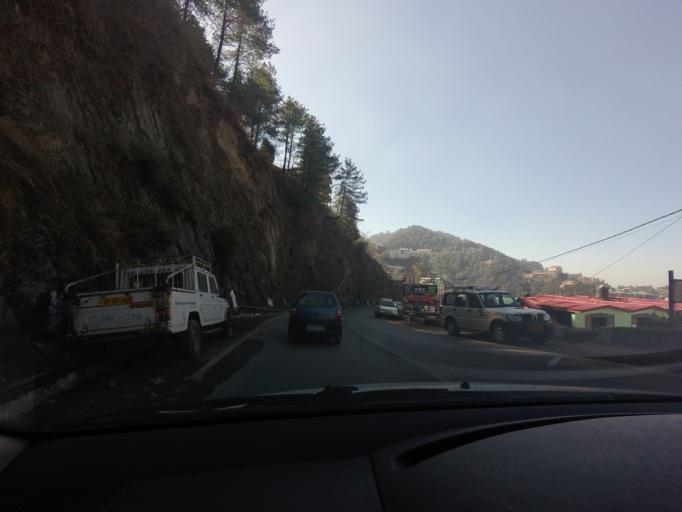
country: IN
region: Himachal Pradesh
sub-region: Shimla
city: Shimla
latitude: 31.1078
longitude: 77.1982
